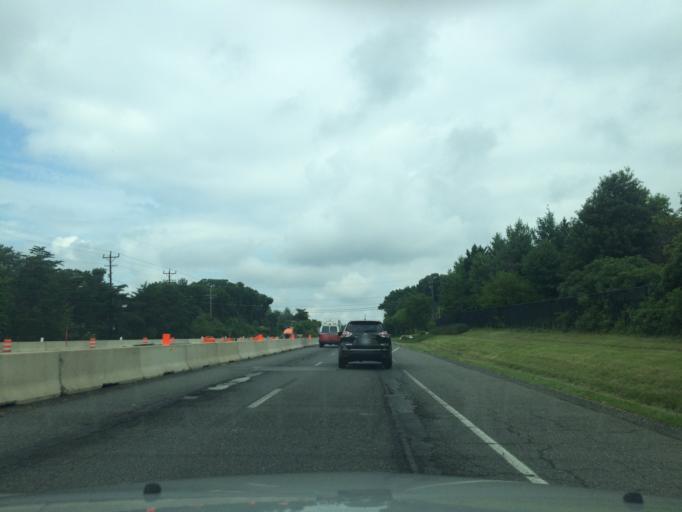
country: US
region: Maryland
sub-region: Prince George's County
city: District Heights
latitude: 38.8489
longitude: -76.9010
